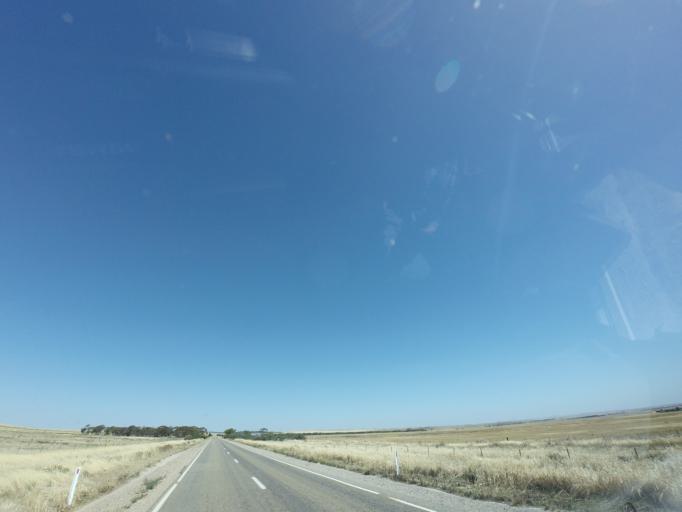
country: AU
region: South Australia
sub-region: Peterborough
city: Peterborough
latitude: -32.9572
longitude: 138.7959
